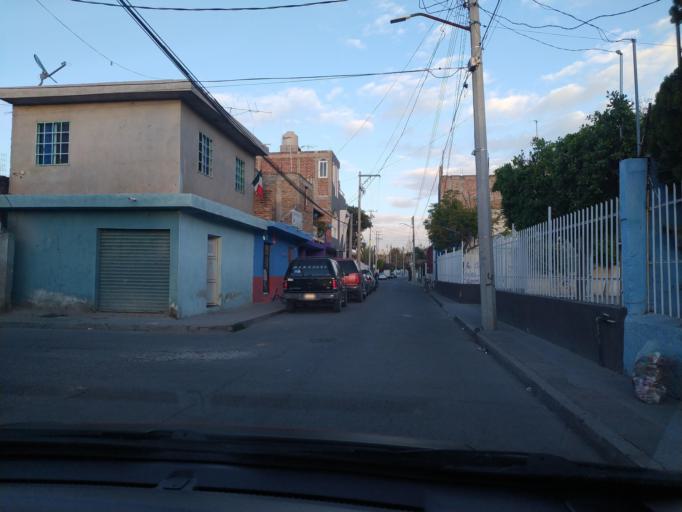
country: MX
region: Guanajuato
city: San Francisco del Rincon
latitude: 21.0064
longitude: -101.8538
